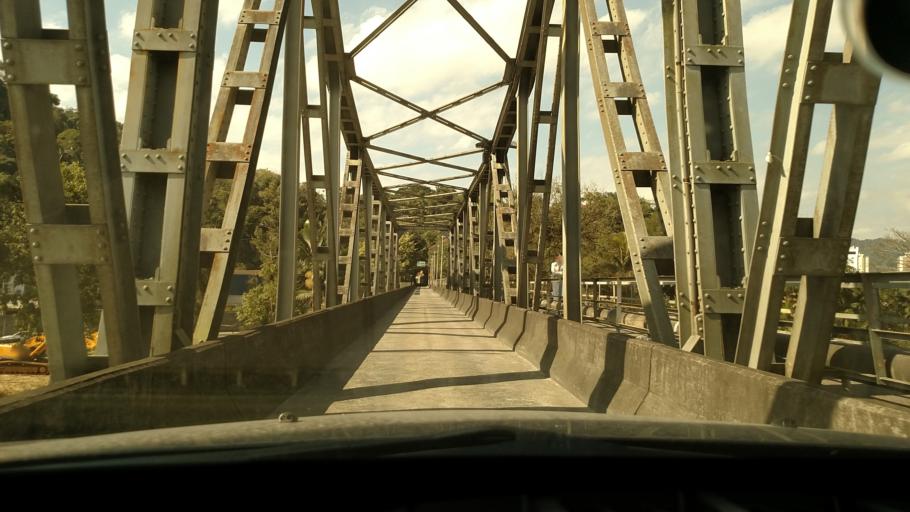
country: BR
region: Santa Catarina
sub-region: Blumenau
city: Blumenau
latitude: -26.9129
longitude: -49.0678
